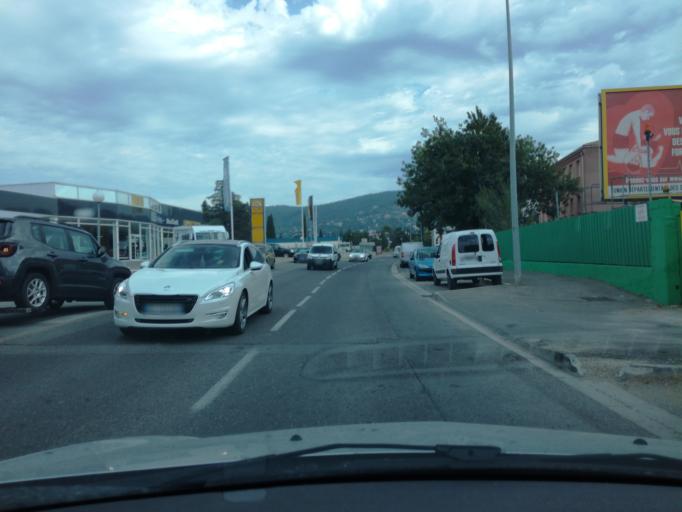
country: FR
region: Provence-Alpes-Cote d'Azur
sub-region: Departement du Var
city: Draguignan
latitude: 43.5292
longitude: 6.4490
